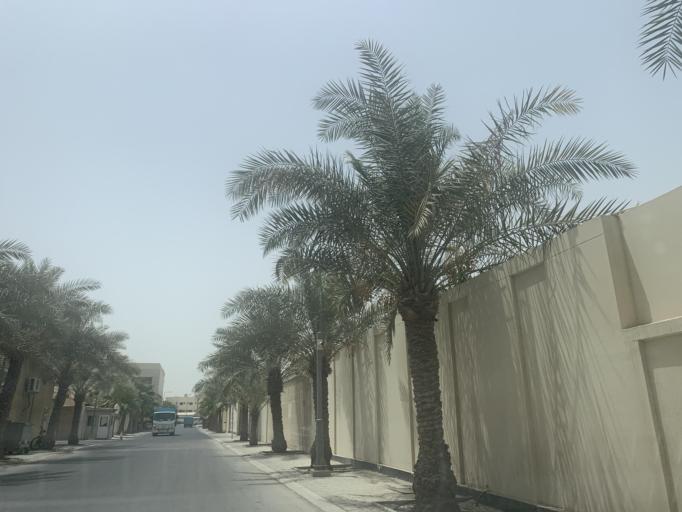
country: BH
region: Manama
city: Jidd Hafs
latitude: 26.2091
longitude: 50.5401
